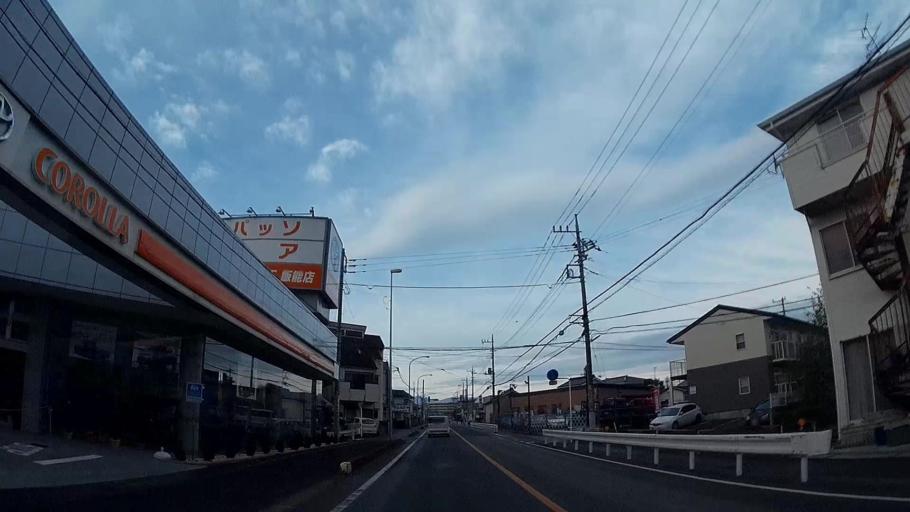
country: JP
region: Saitama
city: Hanno
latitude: 35.8458
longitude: 139.3595
